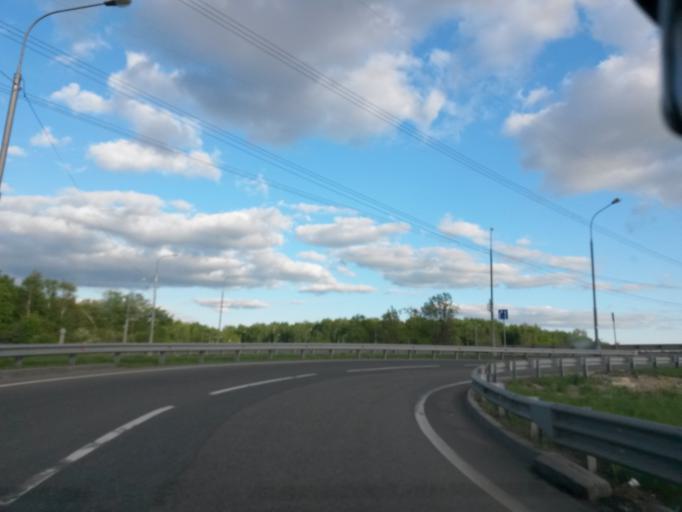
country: RU
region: Moskovskaya
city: Vostryakovo
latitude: 55.6632
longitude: 37.4336
